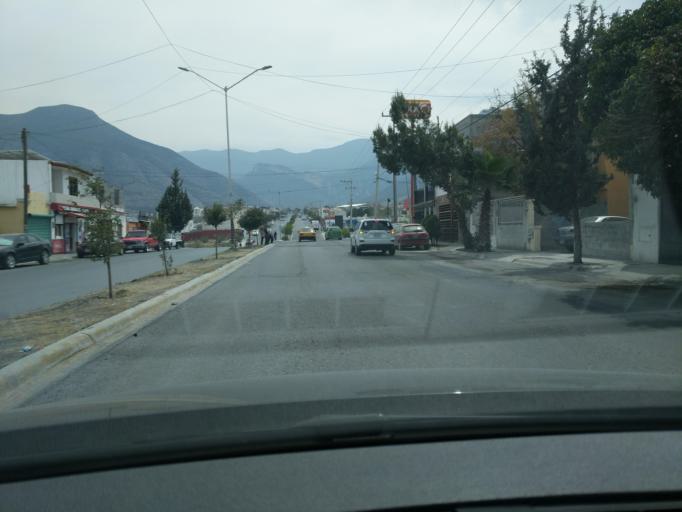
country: MX
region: Coahuila
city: Saltillo
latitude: 25.3543
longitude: -101.0158
